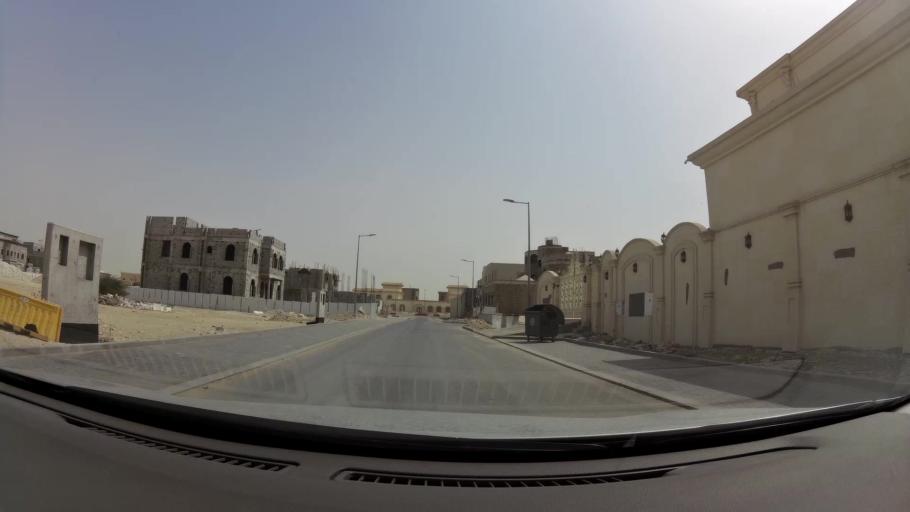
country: QA
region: Baladiyat ar Rayyan
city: Ar Rayyan
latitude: 25.2605
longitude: 51.3688
